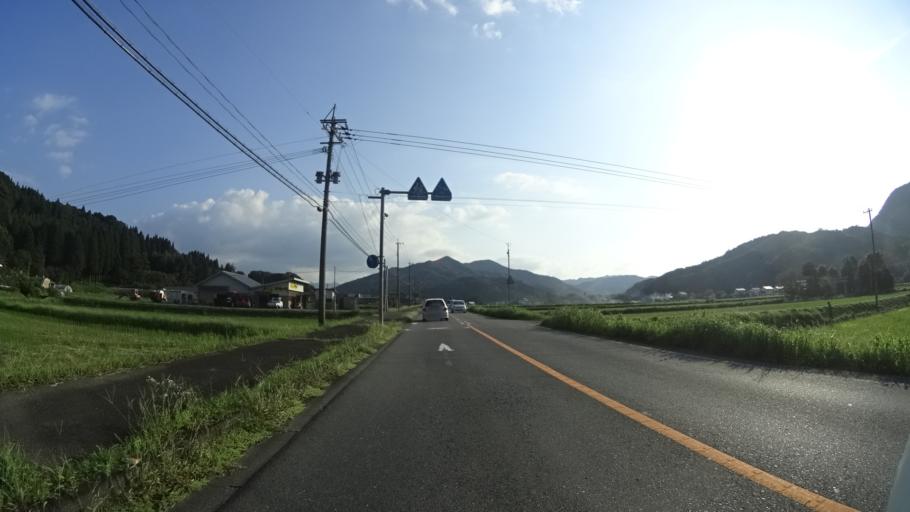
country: JP
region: Oita
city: Bungo-Takada-shi
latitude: 33.4590
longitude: 131.3305
